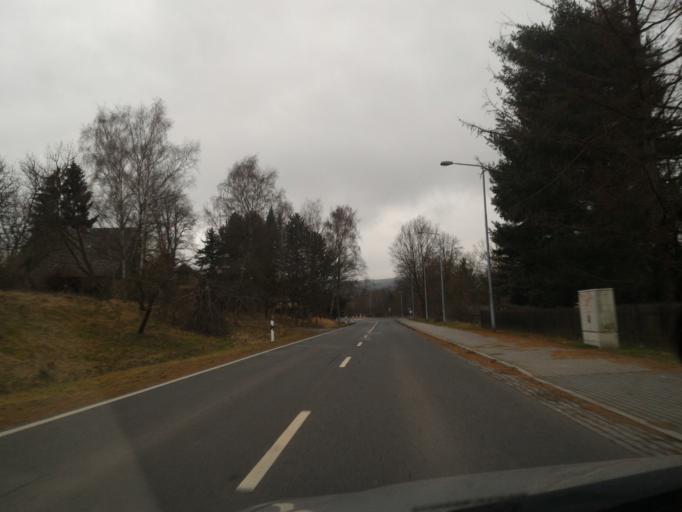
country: DE
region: Saxony
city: Seifhennersdorf
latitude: 50.9253
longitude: 14.6093
